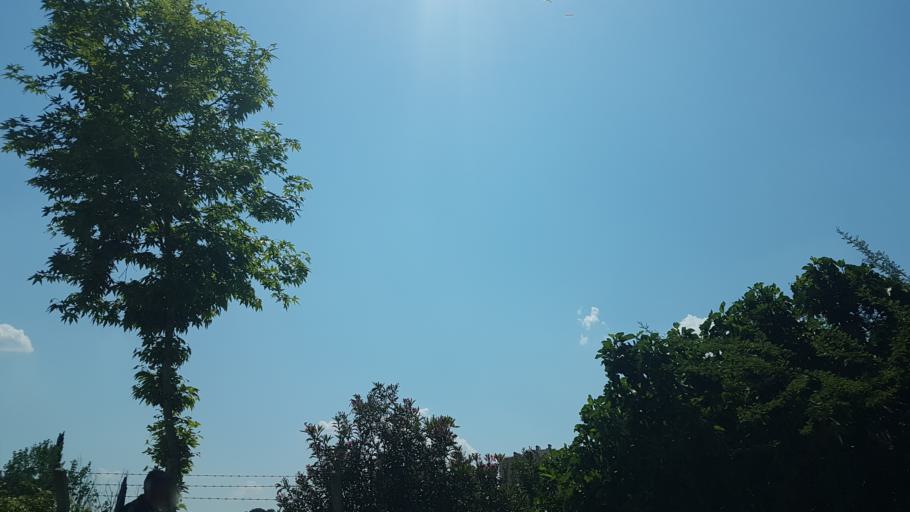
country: TR
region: Adana
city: Adana
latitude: 37.0271
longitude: 35.3602
